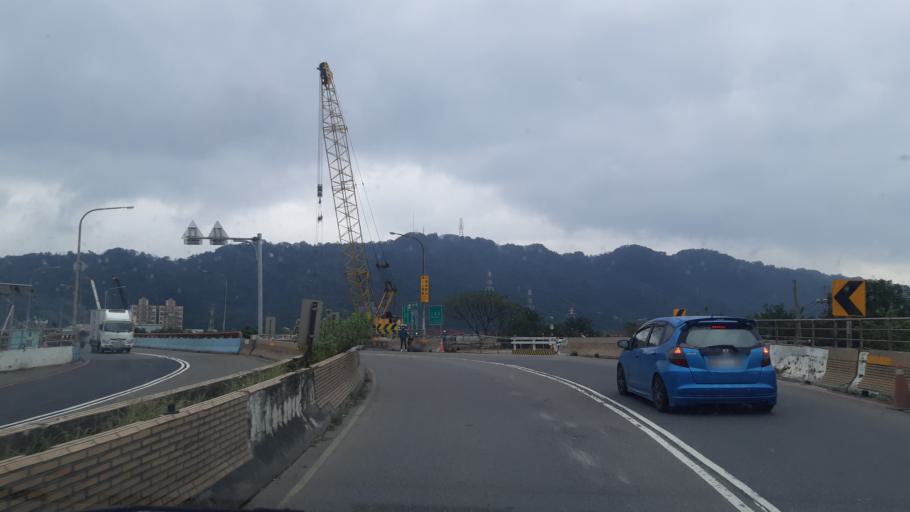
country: TW
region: Taiwan
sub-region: Taoyuan
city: Taoyuan
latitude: 24.9462
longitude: 121.3524
